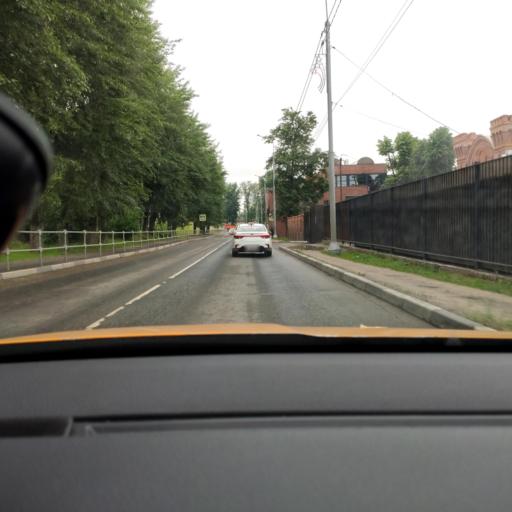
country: RU
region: Moskovskaya
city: Serpukhov
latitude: 54.9151
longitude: 37.4039
